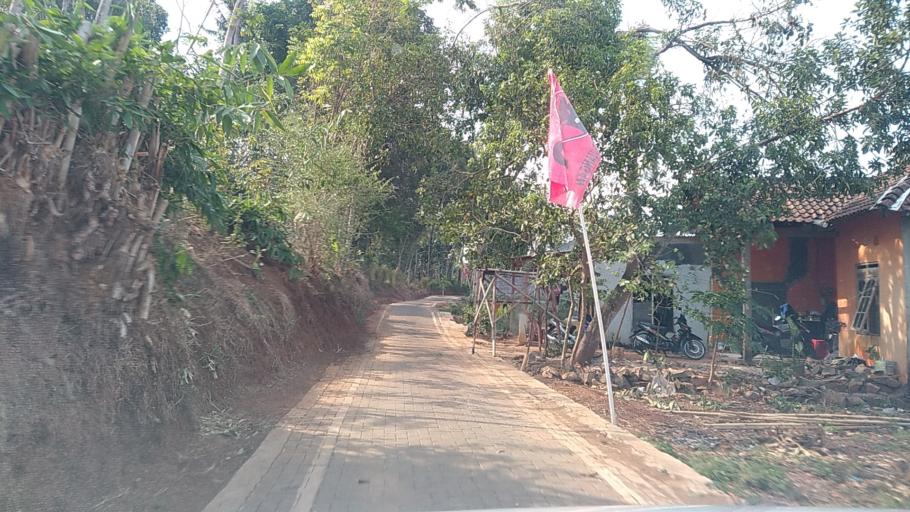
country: ID
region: Central Java
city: Semarang
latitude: -7.0527
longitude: 110.3119
